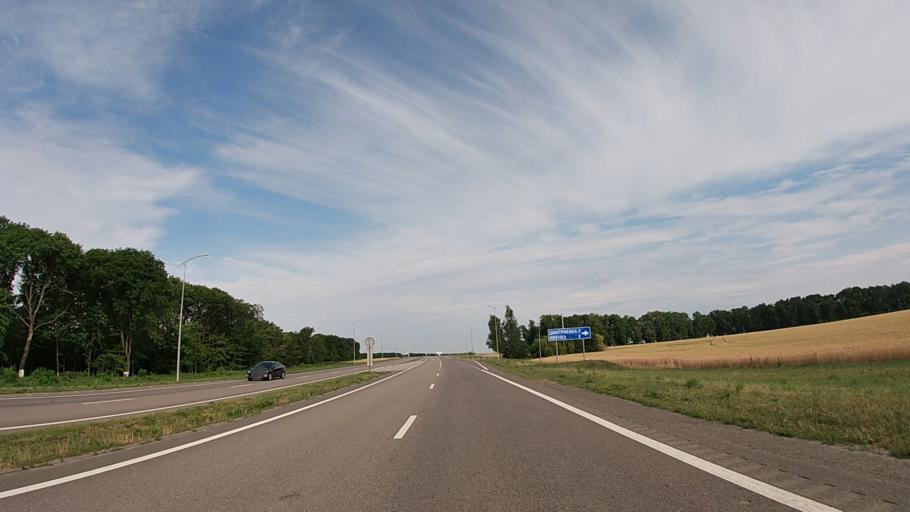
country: RU
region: Belgorod
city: Rakitnoye
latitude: 50.7624
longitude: 35.9598
